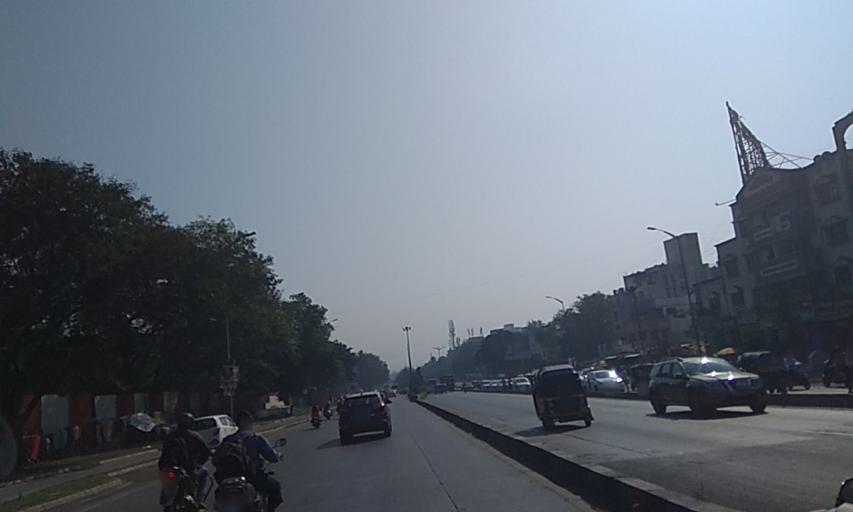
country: IN
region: Maharashtra
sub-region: Pune Division
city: Pune
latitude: 18.5045
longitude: 73.9198
